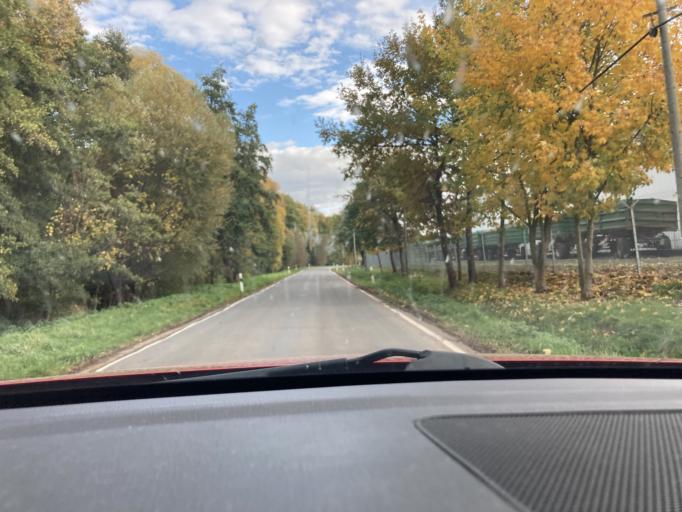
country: DE
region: Thuringia
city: Friedrichsthal
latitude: 51.5197
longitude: 10.5774
